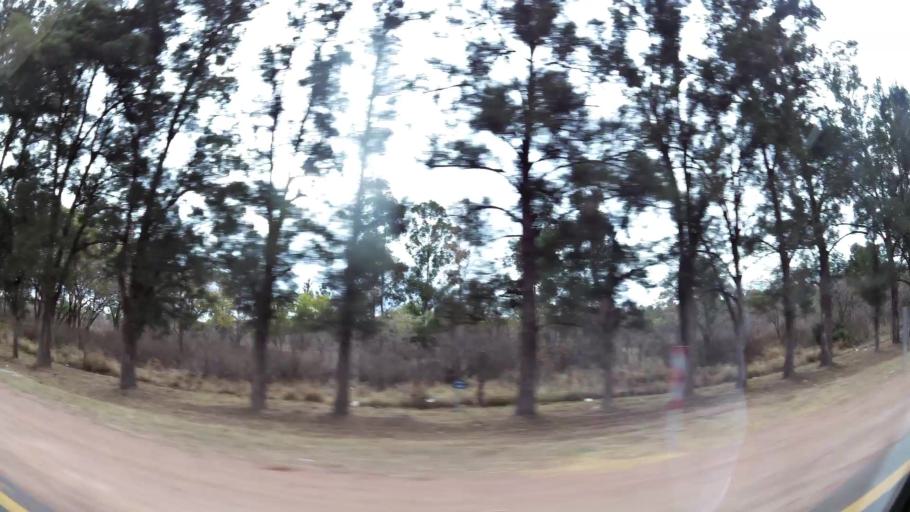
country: ZA
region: Limpopo
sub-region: Waterberg District Municipality
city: Modimolle
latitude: -24.6778
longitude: 28.4391
